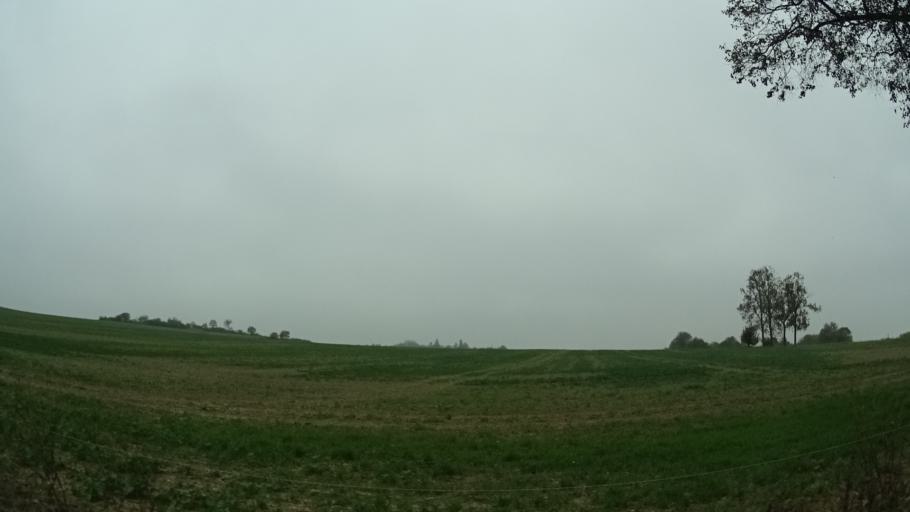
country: DE
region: Thuringia
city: Oberhain
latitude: 50.6400
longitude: 11.1266
